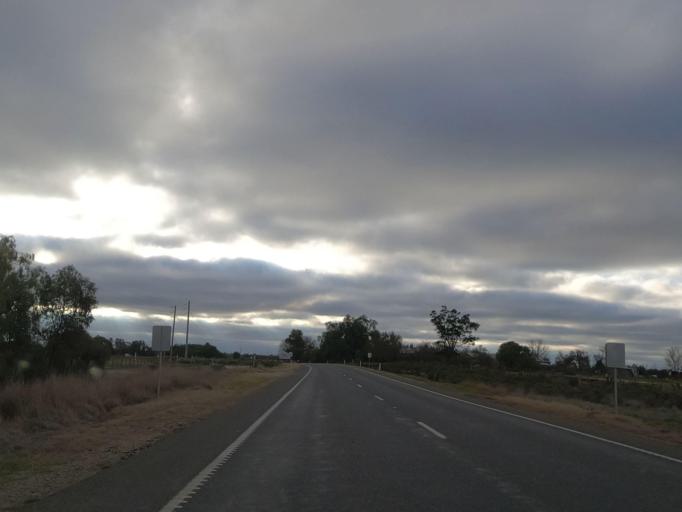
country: AU
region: Victoria
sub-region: Swan Hill
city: Swan Hill
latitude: -35.7253
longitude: 143.8903
